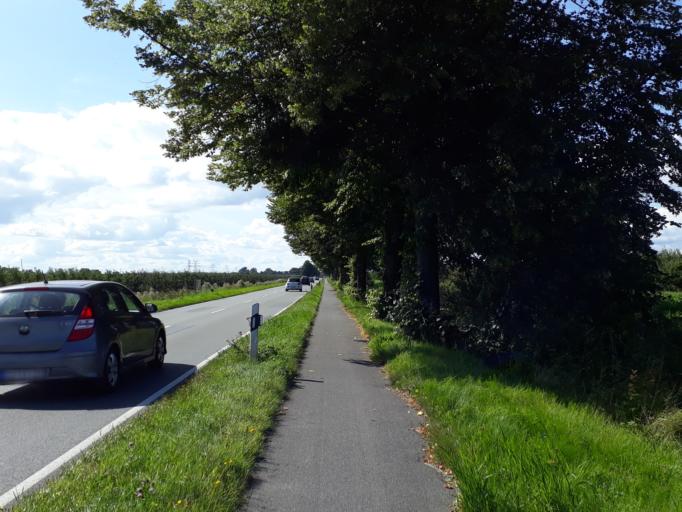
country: DE
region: Lower Saxony
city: Mittelnkirchen
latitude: 53.5395
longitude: 9.6501
